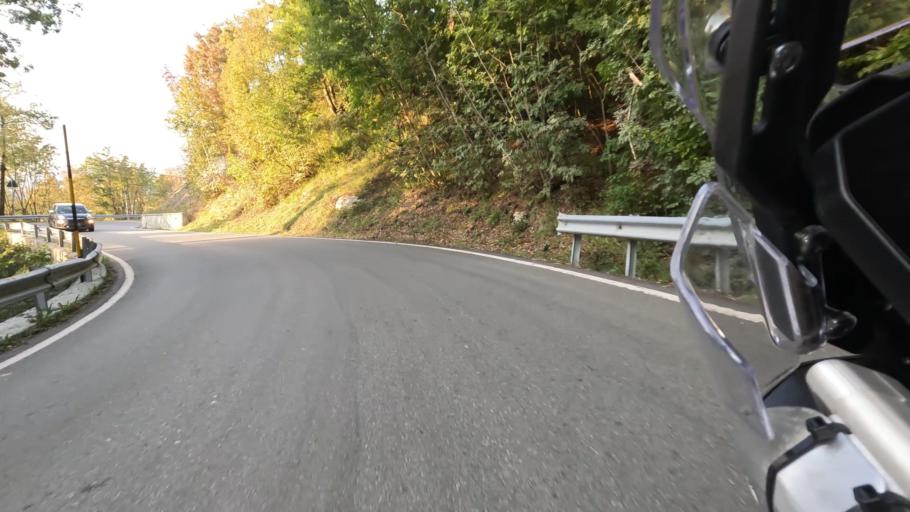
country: IT
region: Liguria
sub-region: Provincia di Savona
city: Sassello
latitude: 44.4881
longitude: 8.4975
